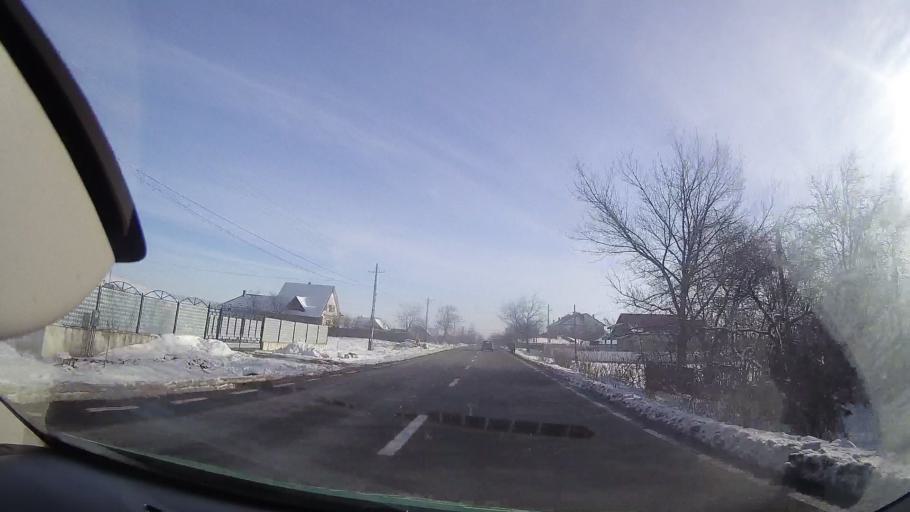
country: RO
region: Neamt
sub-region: Comuna Negresti
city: Negresti
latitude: 47.0616
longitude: 26.3826
